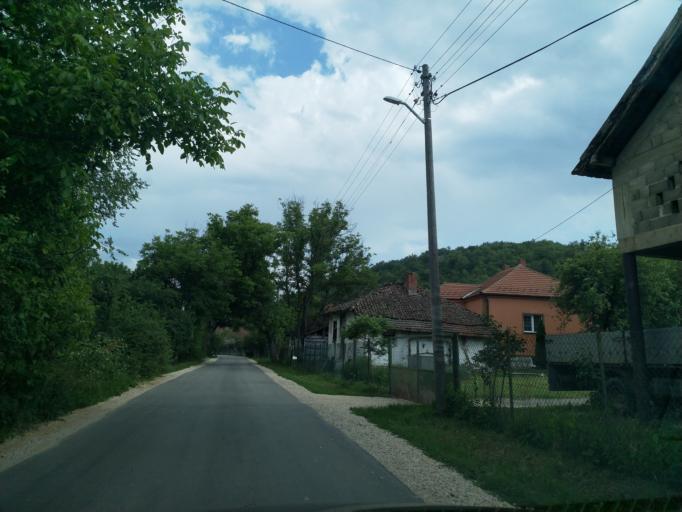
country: RS
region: Central Serbia
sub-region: Borski Okrug
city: Bor
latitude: 44.0171
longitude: 21.9814
